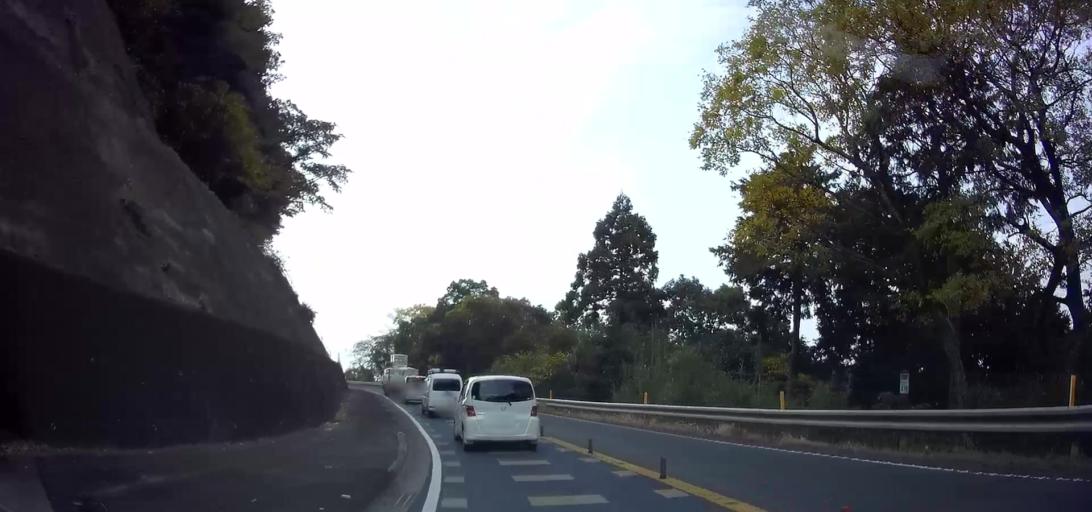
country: JP
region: Nagasaki
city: Shimabara
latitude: 32.7607
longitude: 130.2032
